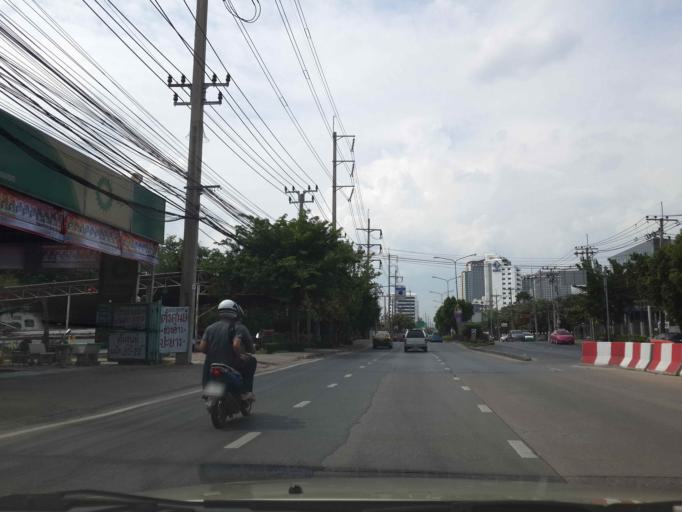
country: TH
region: Bangkok
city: Suan Luang
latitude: 13.7459
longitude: 100.6435
